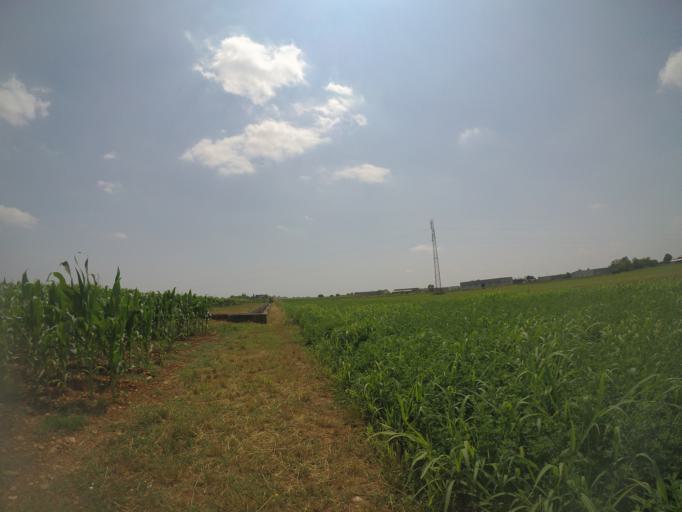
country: IT
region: Friuli Venezia Giulia
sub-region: Provincia di Udine
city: Bertiolo
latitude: 45.9549
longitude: 13.0611
